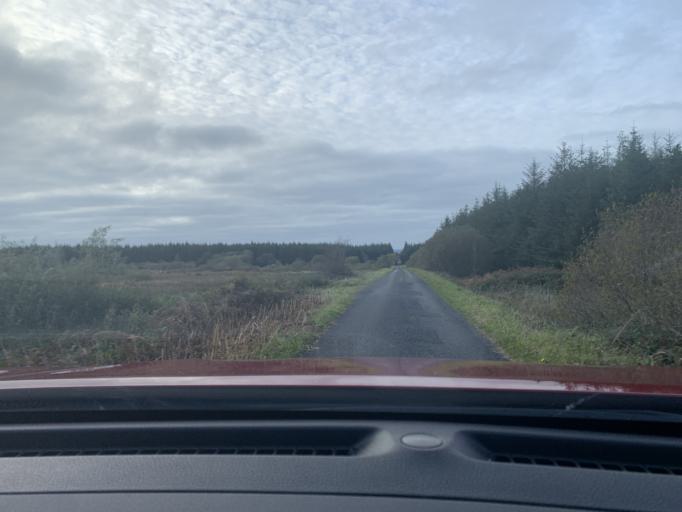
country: IE
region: Connaught
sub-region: Roscommon
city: Ballaghaderreen
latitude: 53.9662
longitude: -8.6127
